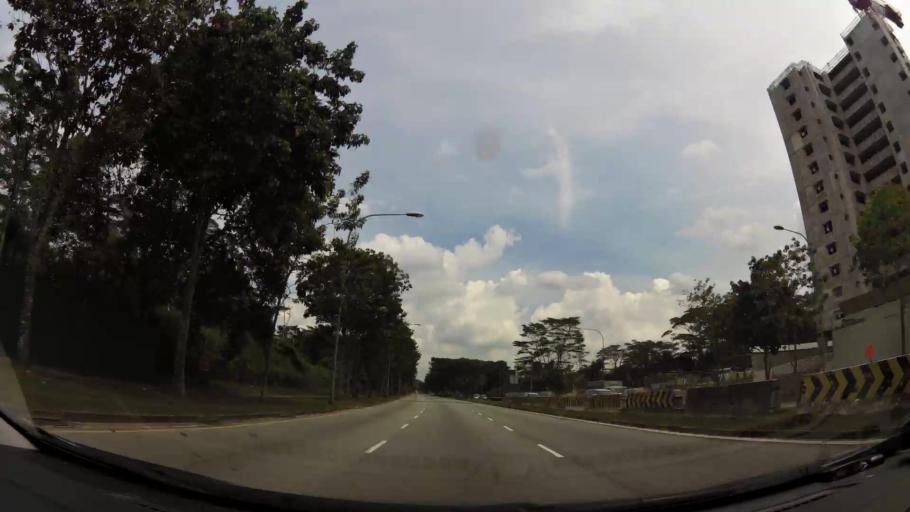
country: MY
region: Johor
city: Johor Bahru
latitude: 1.3600
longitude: 103.7399
